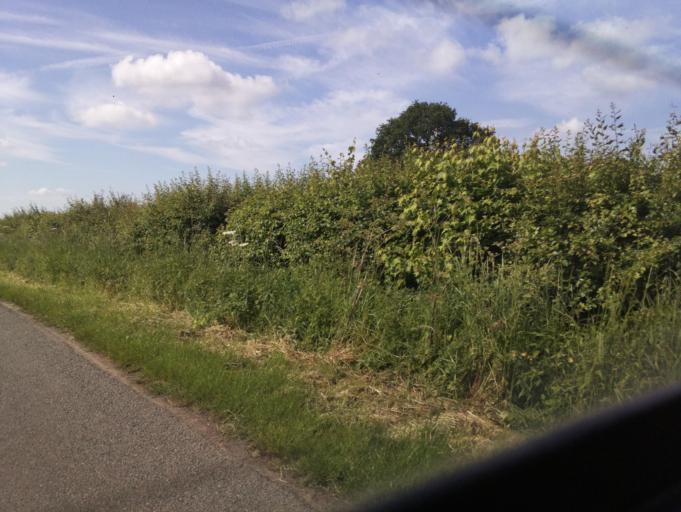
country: GB
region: England
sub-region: Lincolnshire
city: Skellingthorpe
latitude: 53.1387
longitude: -0.6333
